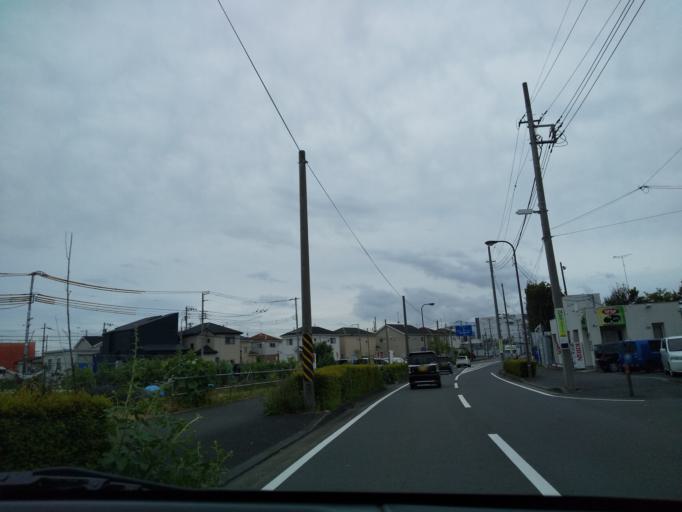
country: JP
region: Tokyo
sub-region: Machida-shi
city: Machida
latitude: 35.5335
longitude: 139.4072
